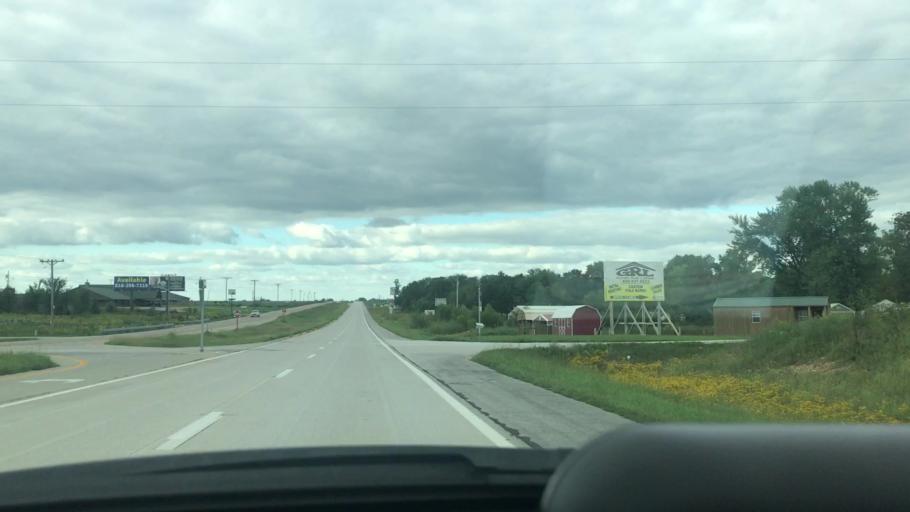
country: US
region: Missouri
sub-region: Benton County
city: Lincoln
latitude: 38.3474
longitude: -93.3400
